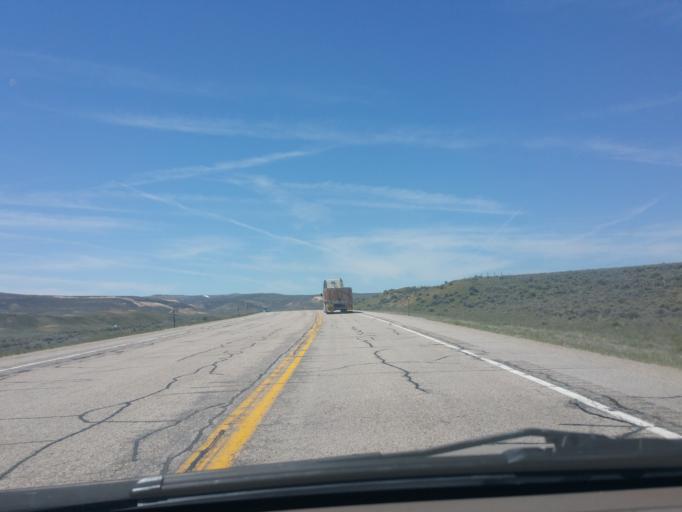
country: US
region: Wyoming
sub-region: Lincoln County
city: Kemmerer
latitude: 41.8146
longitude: -110.6671
